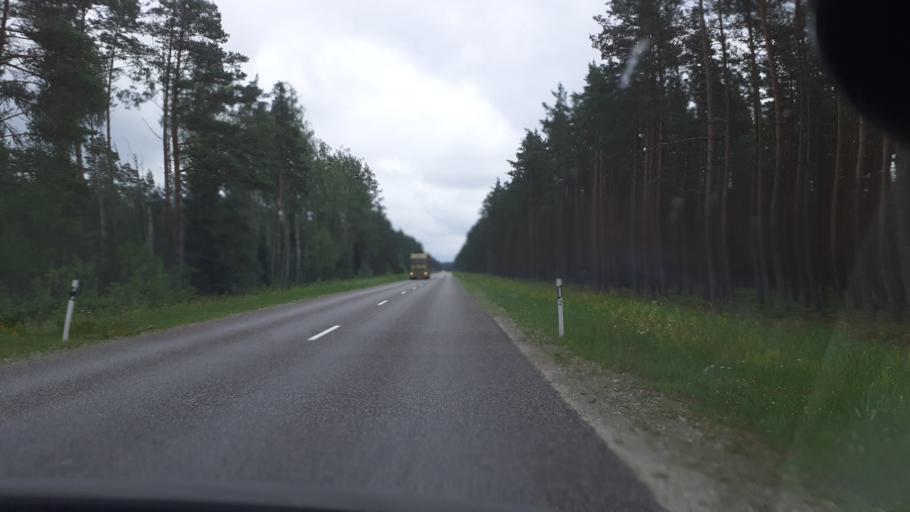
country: LV
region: Ventspils Rajons
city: Piltene
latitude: 57.1306
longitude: 21.7310
